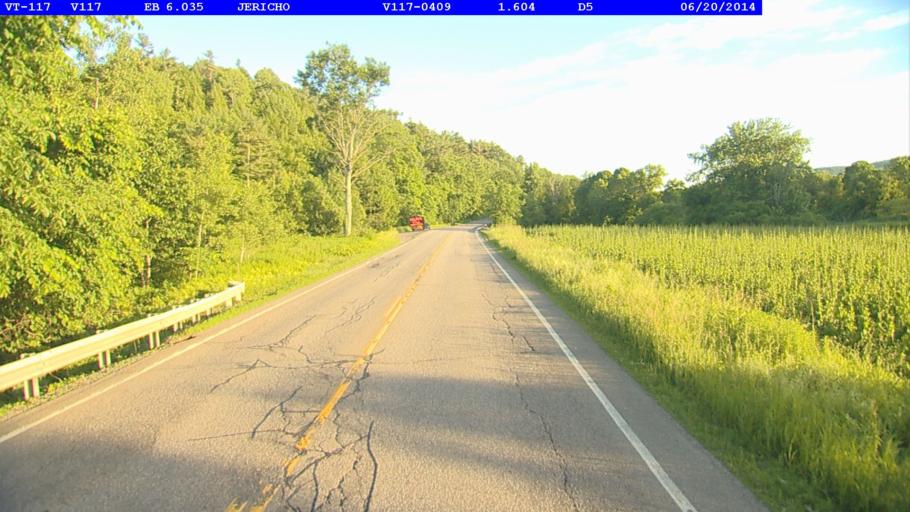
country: US
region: Vermont
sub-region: Chittenden County
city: Williston
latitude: 44.4520
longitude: -73.0179
